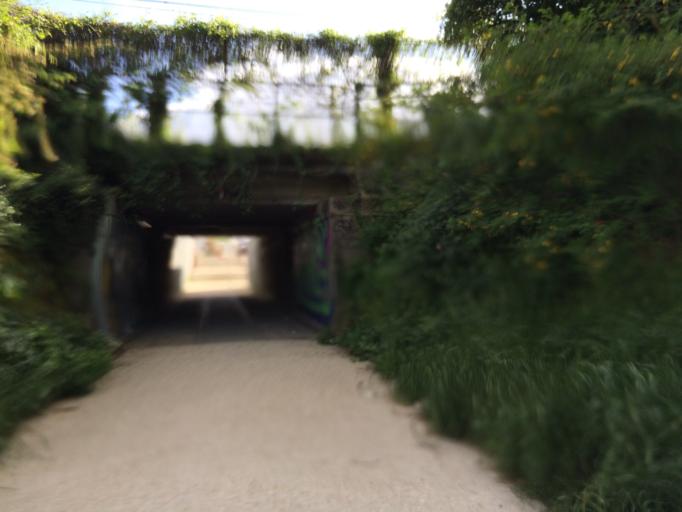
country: FR
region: Ile-de-France
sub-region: Departement de l'Essonne
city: Ris-Orangis
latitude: 48.6579
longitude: 2.4188
